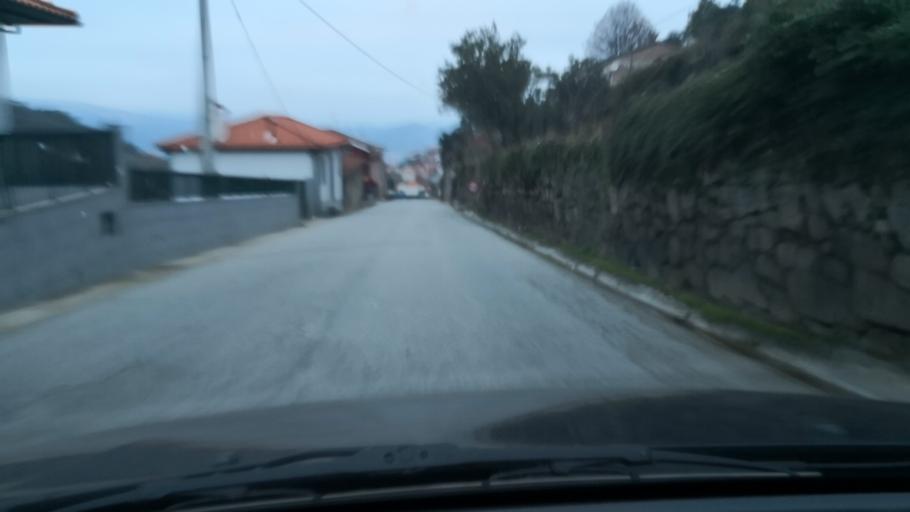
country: PT
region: Viseu
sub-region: Lamego
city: Lamego
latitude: 41.1235
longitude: -7.8025
